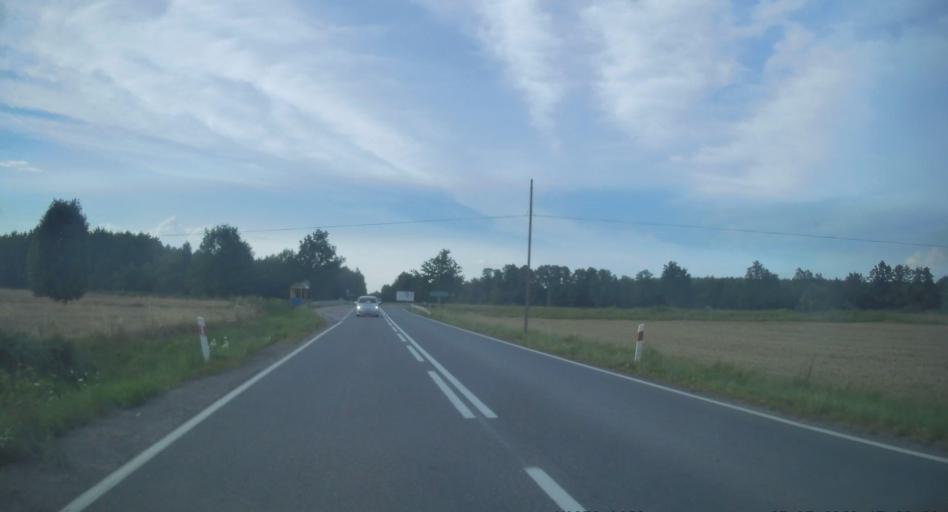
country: PL
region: Lesser Poland Voivodeship
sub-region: Powiat brzeski
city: Szczurowa
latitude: 50.0770
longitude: 20.6338
